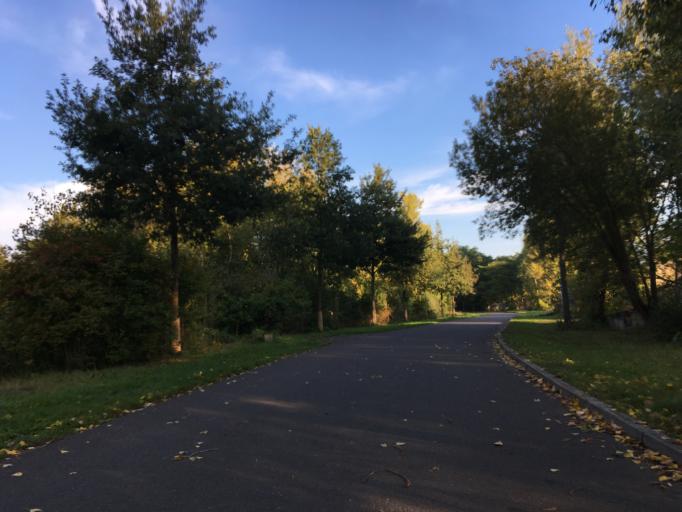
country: DE
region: Brandenburg
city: Frankfurt (Oder)
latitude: 52.3592
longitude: 14.5486
